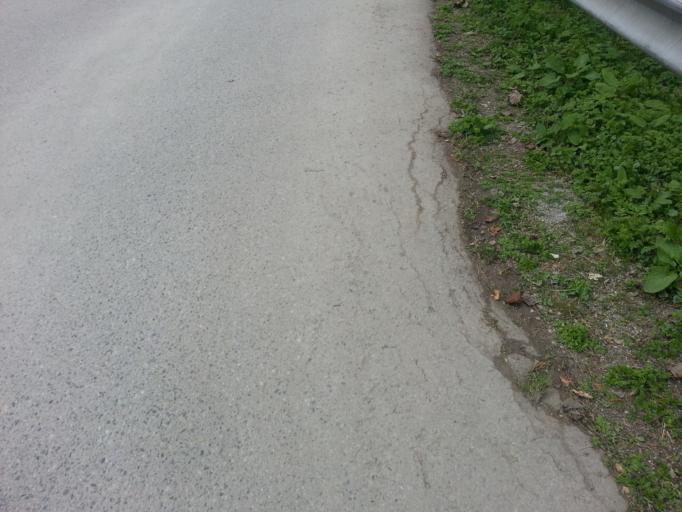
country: NO
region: Akershus
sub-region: Baerum
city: Lysaker
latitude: 59.9060
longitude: 10.6372
